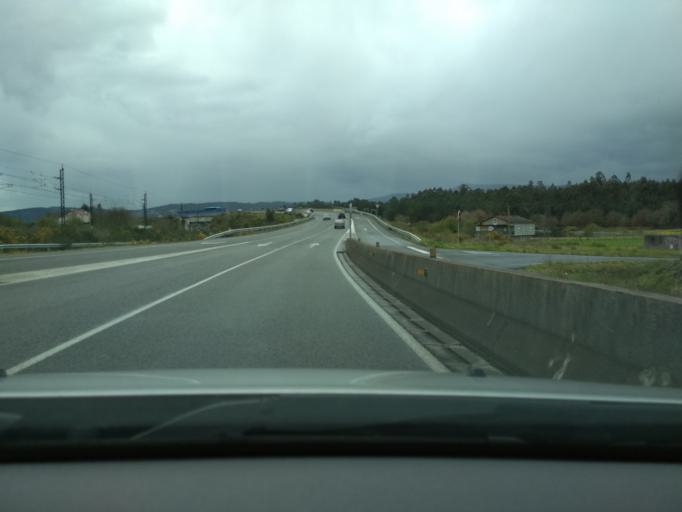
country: ES
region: Galicia
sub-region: Provincia da Coruna
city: Padron
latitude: 42.7922
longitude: -8.6471
